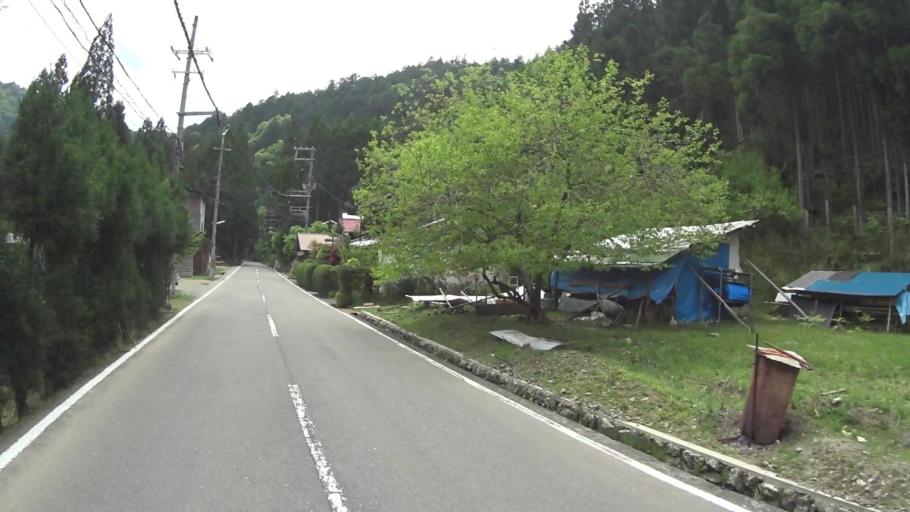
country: JP
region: Kyoto
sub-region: Kyoto-shi
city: Kamigyo-ku
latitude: 35.1968
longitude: 135.7103
